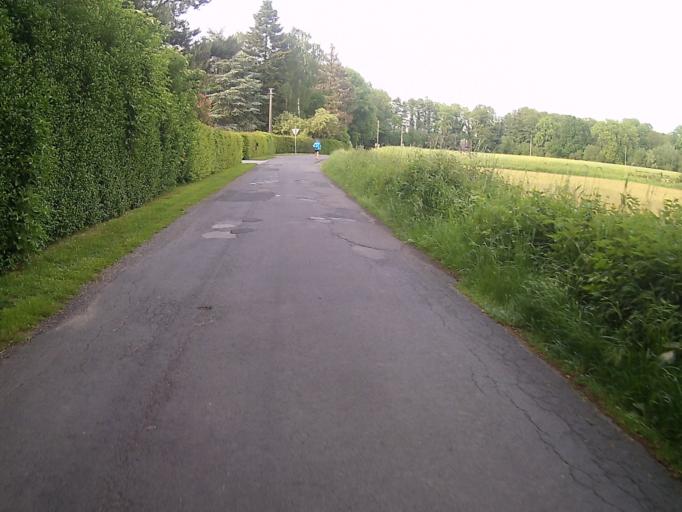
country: DE
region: North Rhine-Westphalia
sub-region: Regierungsbezirk Dusseldorf
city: Krefeld
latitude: 51.4023
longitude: 6.5358
